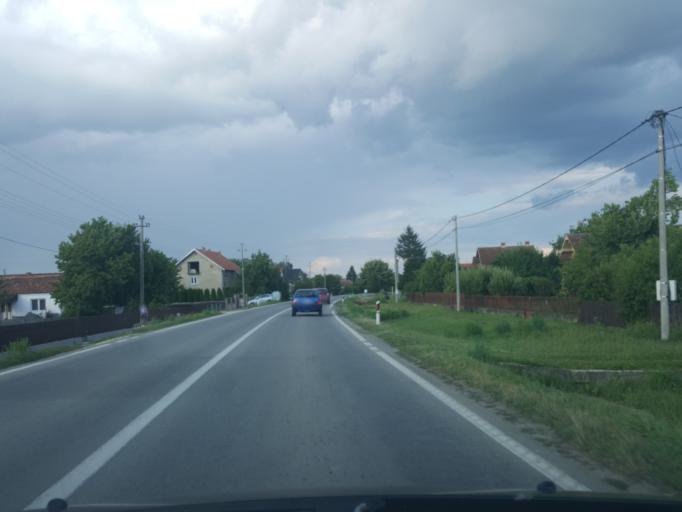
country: RS
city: Novo Selo
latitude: 44.6677
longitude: 19.3375
